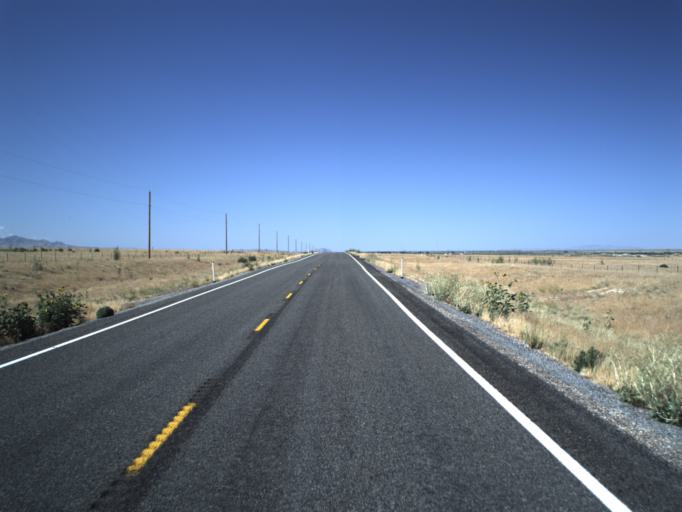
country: US
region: Utah
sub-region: Millard County
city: Delta
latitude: 39.6213
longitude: -112.3143
